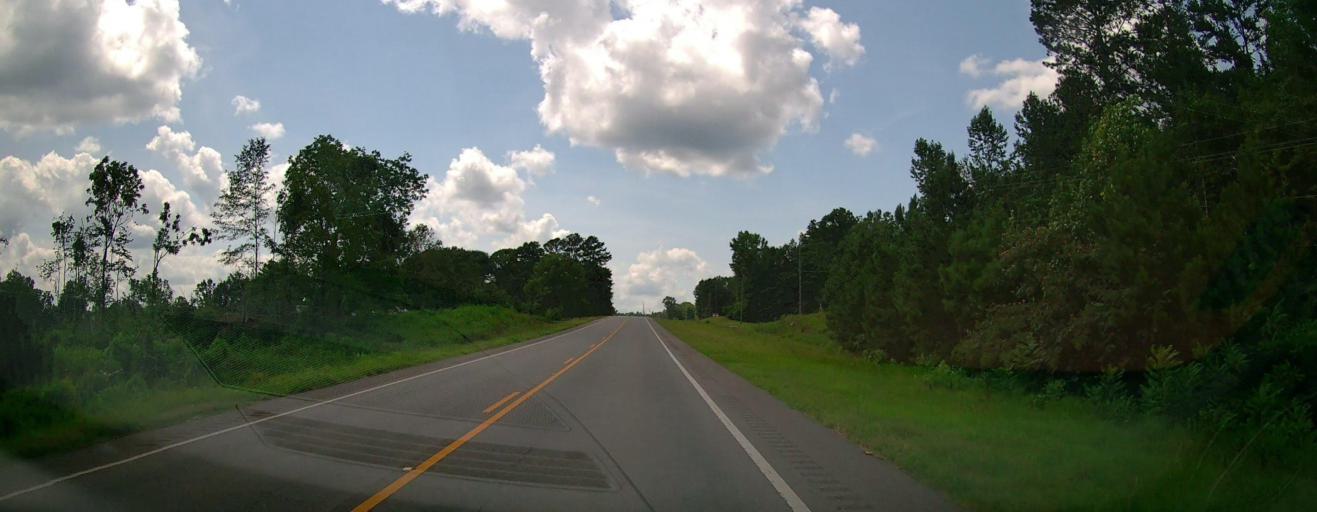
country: US
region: Alabama
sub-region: Cleburne County
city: Heflin
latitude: 33.5805
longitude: -85.4659
